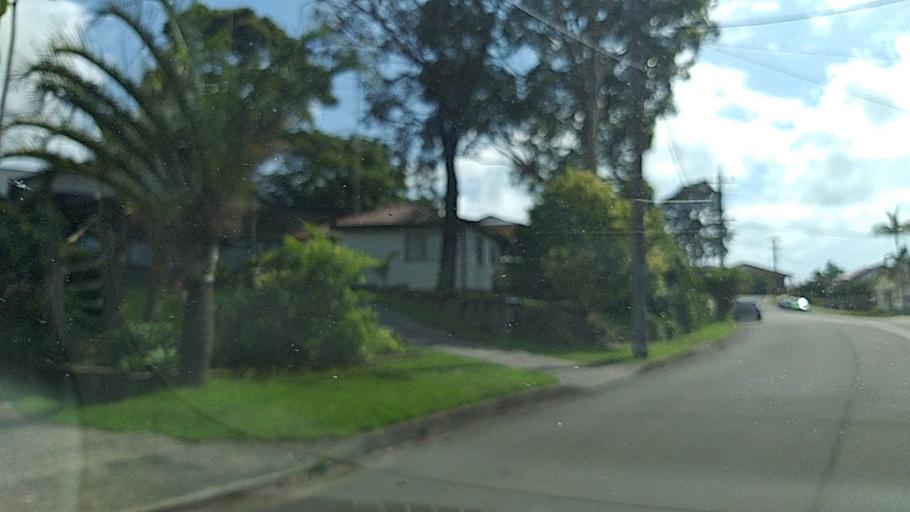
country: AU
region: New South Wales
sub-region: Wollongong
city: Corrimal
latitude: -34.3747
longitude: 150.8905
